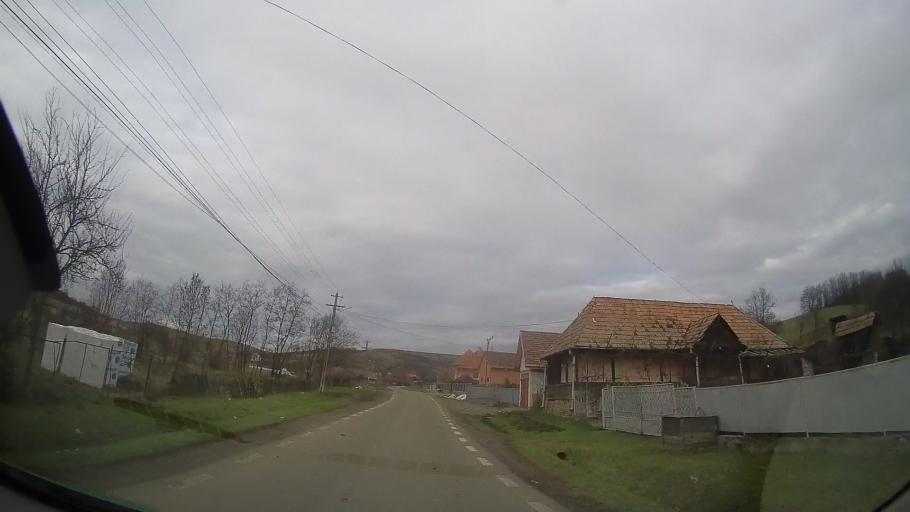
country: RO
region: Mures
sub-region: Comuna Cozma
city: Cozma
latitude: 46.8105
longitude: 24.5153
